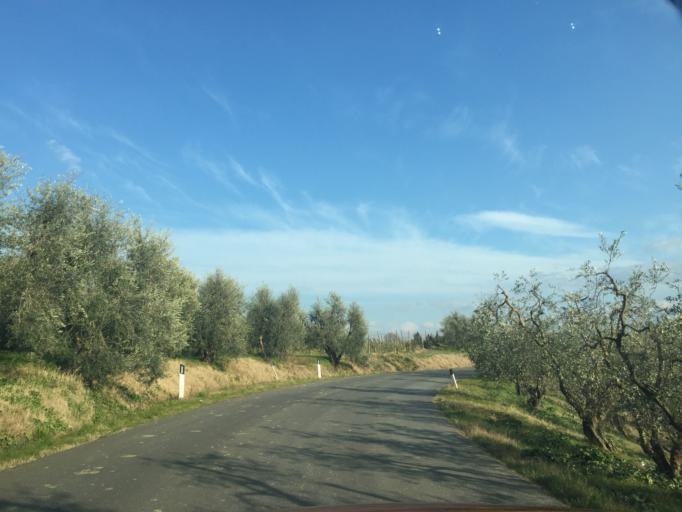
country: IT
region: Tuscany
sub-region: Province of Florence
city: Lazzeretto
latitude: 43.7631
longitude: 10.8495
